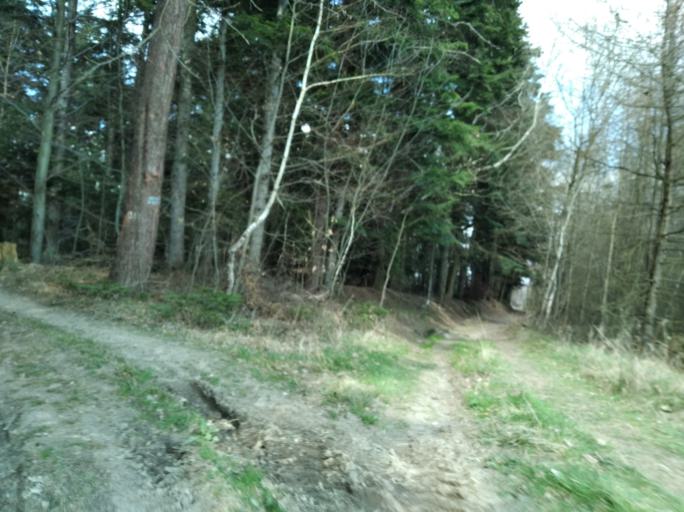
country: PL
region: Subcarpathian Voivodeship
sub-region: Powiat strzyzowski
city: Strzyzow
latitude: 49.8294
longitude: 21.8060
